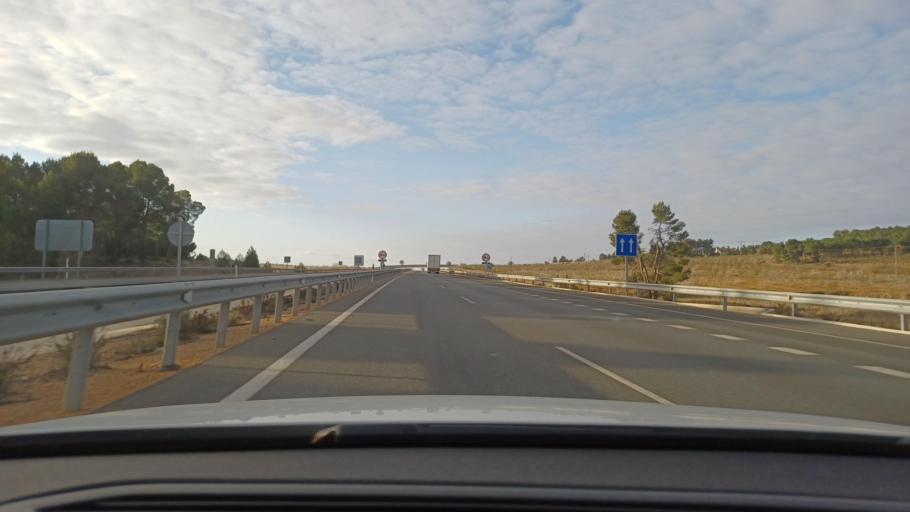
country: ES
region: Valencia
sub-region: Provincia de Valencia
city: La Font de la Figuera
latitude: 38.7747
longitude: -0.8929
